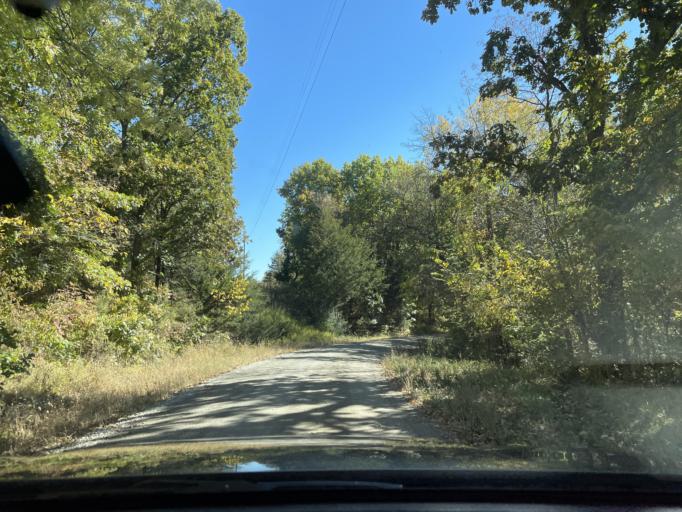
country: US
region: Missouri
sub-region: Andrew County
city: Savannah
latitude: 39.9399
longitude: -94.8708
